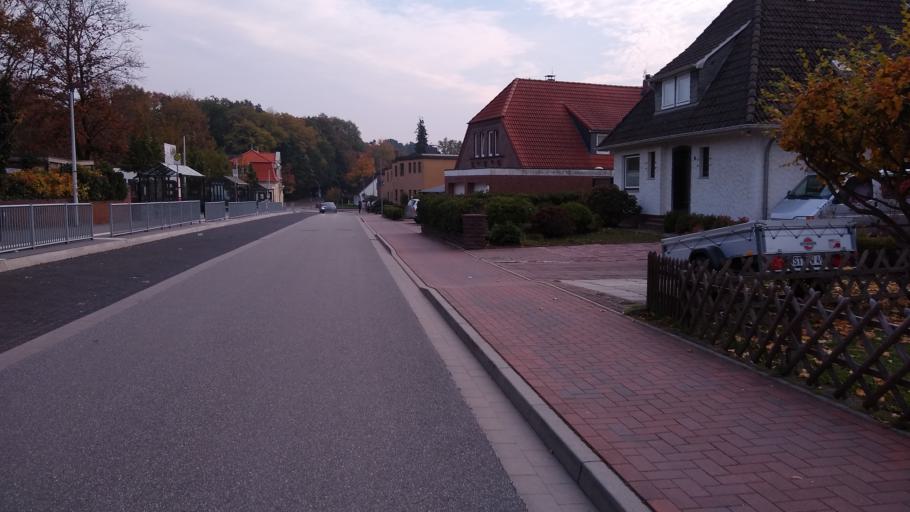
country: DE
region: Lower Saxony
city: Rastede
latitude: 53.2439
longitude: 8.1955
